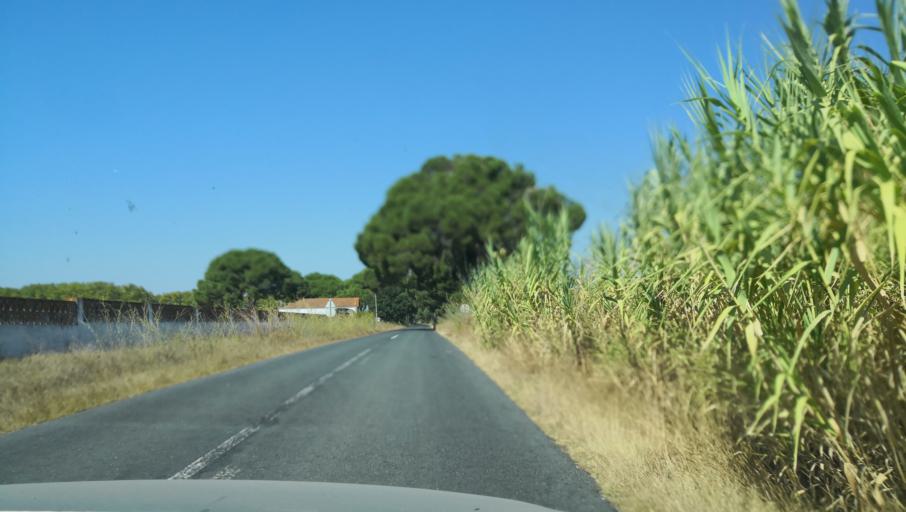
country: PT
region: Setubal
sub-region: Alcacer do Sal
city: Alcacer do Sal
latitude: 38.2790
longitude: -8.3950
